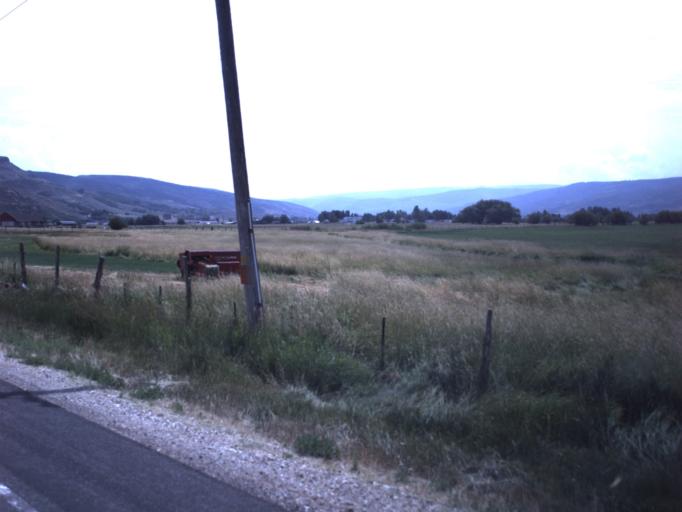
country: US
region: Utah
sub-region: Summit County
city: Francis
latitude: 40.6105
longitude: -111.2719
